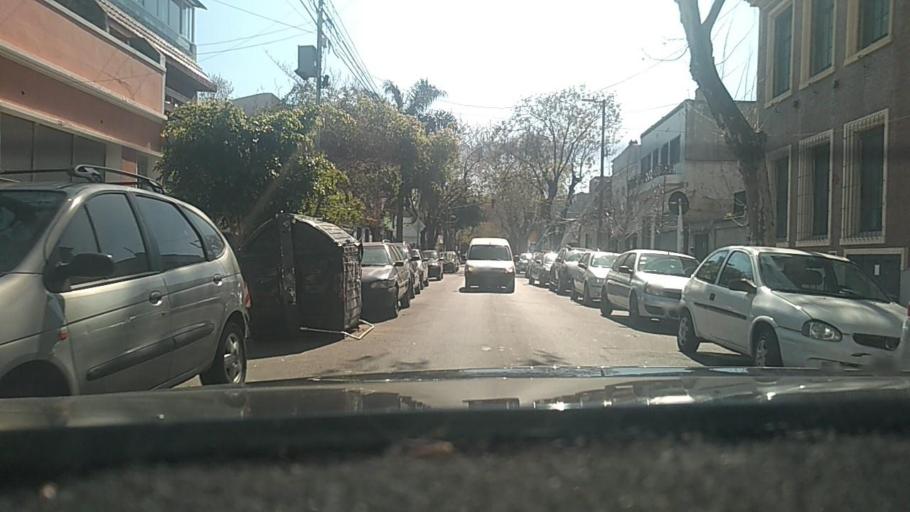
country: AR
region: Buenos Aires F.D.
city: Villa Santa Rita
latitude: -34.6041
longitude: -58.4819
